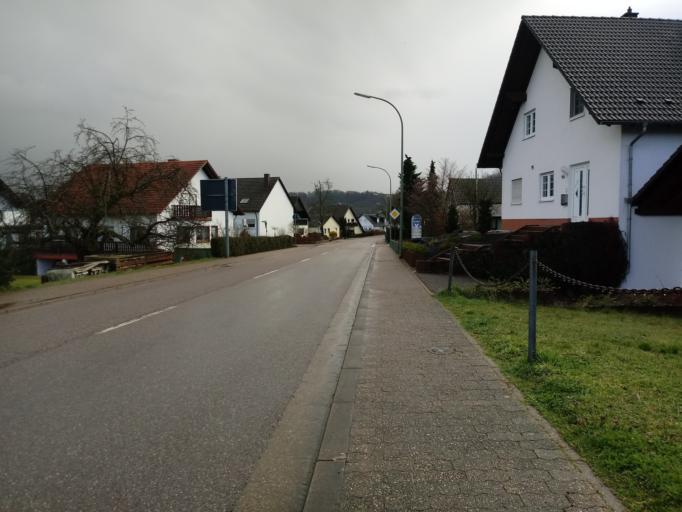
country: DE
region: Saarland
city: Uberherrn
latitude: 49.2750
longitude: 6.7097
